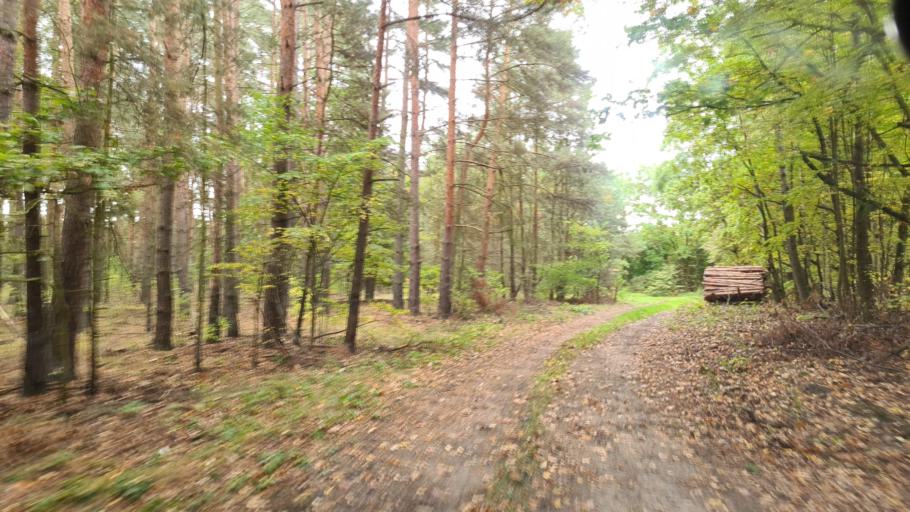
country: DE
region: Brandenburg
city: Altdobern
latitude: 51.6742
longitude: 14.1074
